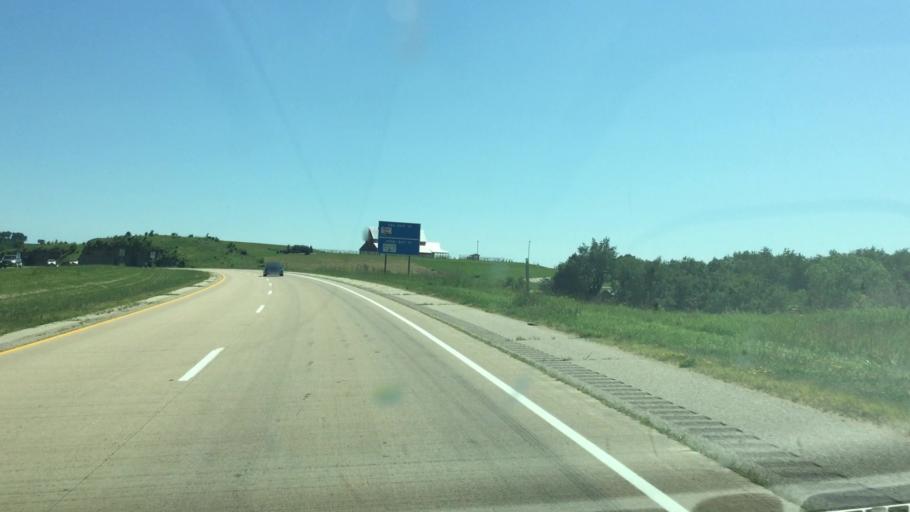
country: US
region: Wisconsin
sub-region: Iowa County
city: Mineral Point
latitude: 42.8599
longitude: -90.2034
